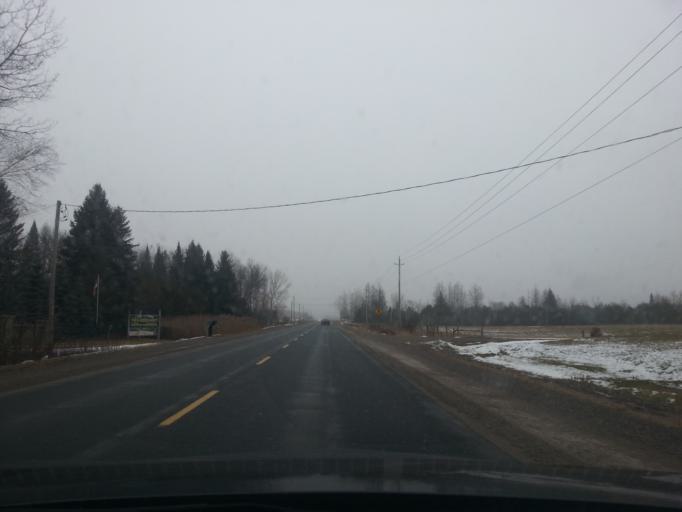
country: CA
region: Ontario
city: Omemee
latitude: 44.1646
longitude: -78.6981
